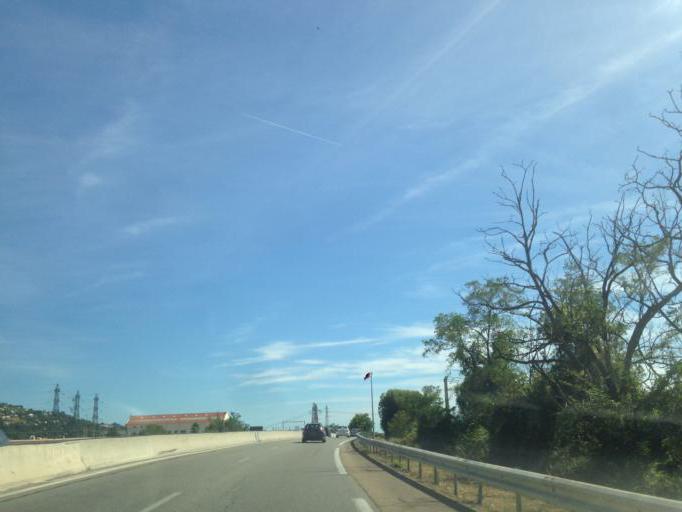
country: FR
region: Provence-Alpes-Cote d'Azur
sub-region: Departement des Alpes-Maritimes
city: La Gaude
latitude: 43.7233
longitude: 7.1860
